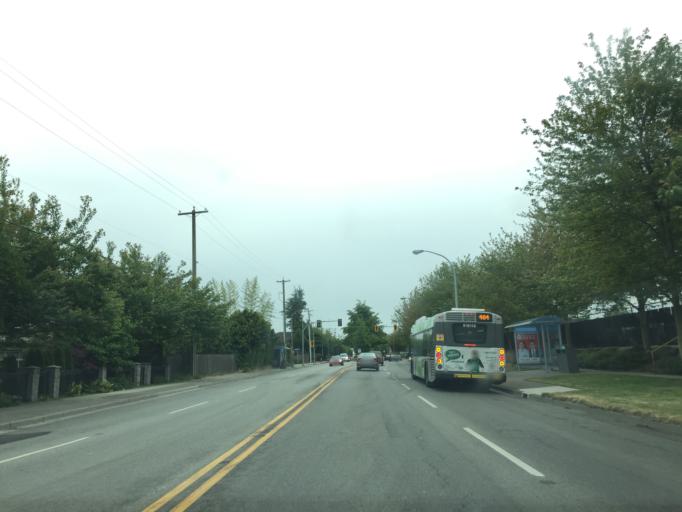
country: CA
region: British Columbia
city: Ladner
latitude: 49.1333
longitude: -123.1013
